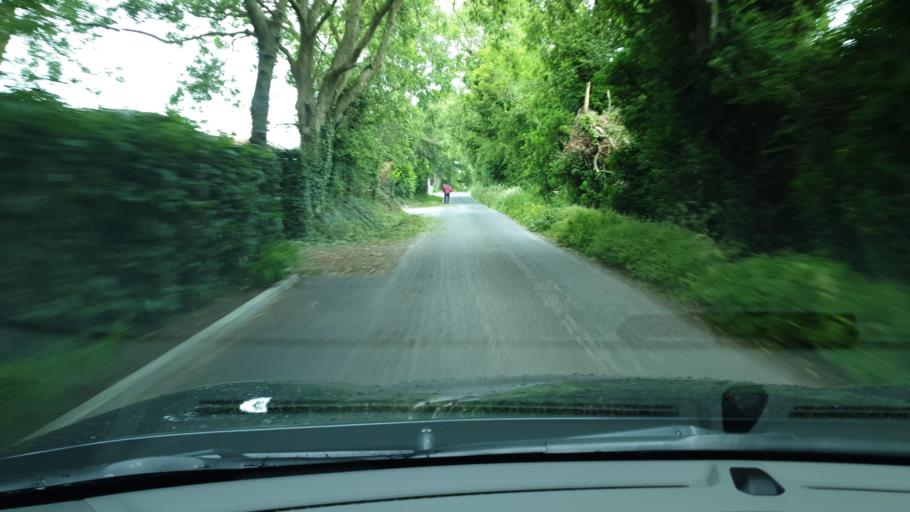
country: IE
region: Leinster
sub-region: An Mhi
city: Ashbourne
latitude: 53.5253
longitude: -6.3897
